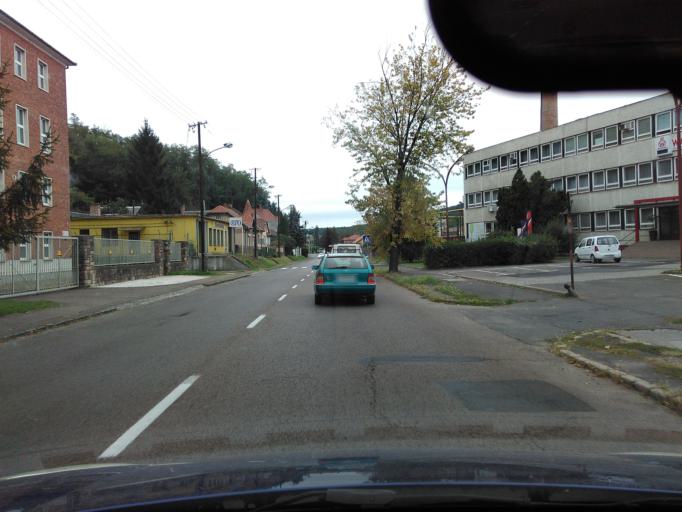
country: HU
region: Nograd
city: Salgotarjan
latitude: 48.0933
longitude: 19.7990
